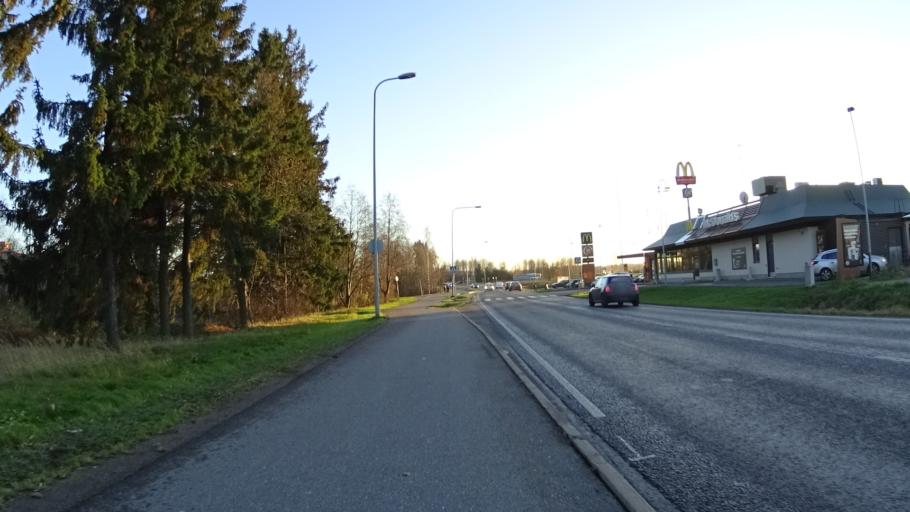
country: FI
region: Uusimaa
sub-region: Helsinki
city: Vantaa
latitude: 60.2712
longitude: 24.9754
